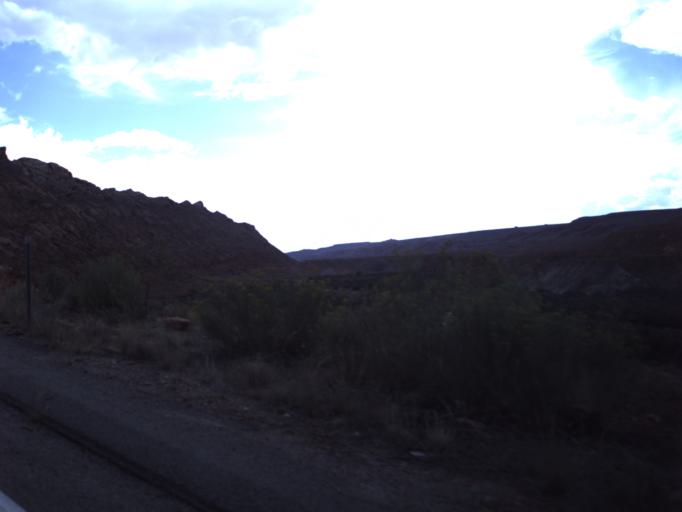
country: US
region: Utah
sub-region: San Juan County
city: Blanding
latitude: 37.2644
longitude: -109.6738
